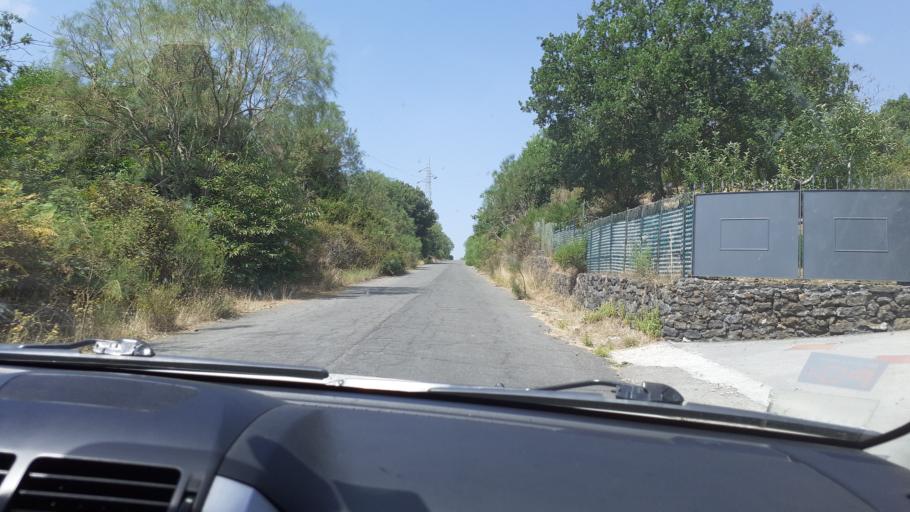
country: IT
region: Sicily
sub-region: Catania
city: Nicolosi
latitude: 37.6474
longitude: 15.0183
